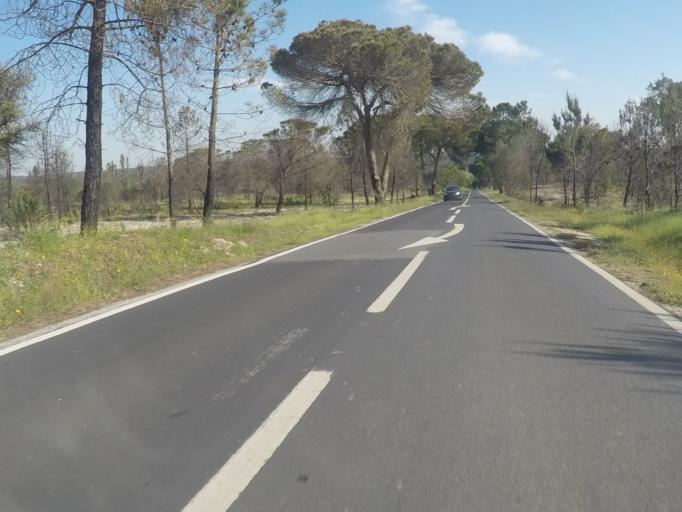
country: PT
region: Setubal
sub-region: Sesimbra
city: Sesimbra
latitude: 38.5190
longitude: -9.1435
